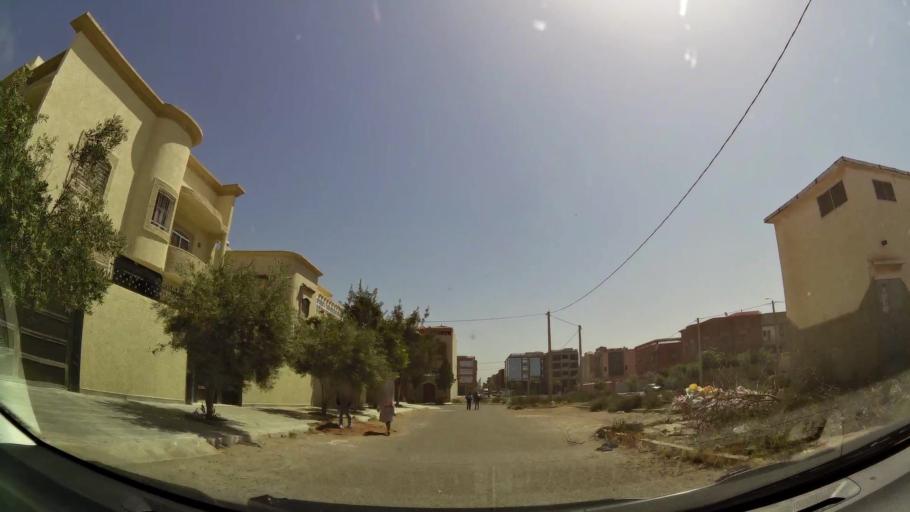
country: MA
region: Souss-Massa-Draa
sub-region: Inezgane-Ait Mellou
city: Inezgane
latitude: 30.3226
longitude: -9.5049
